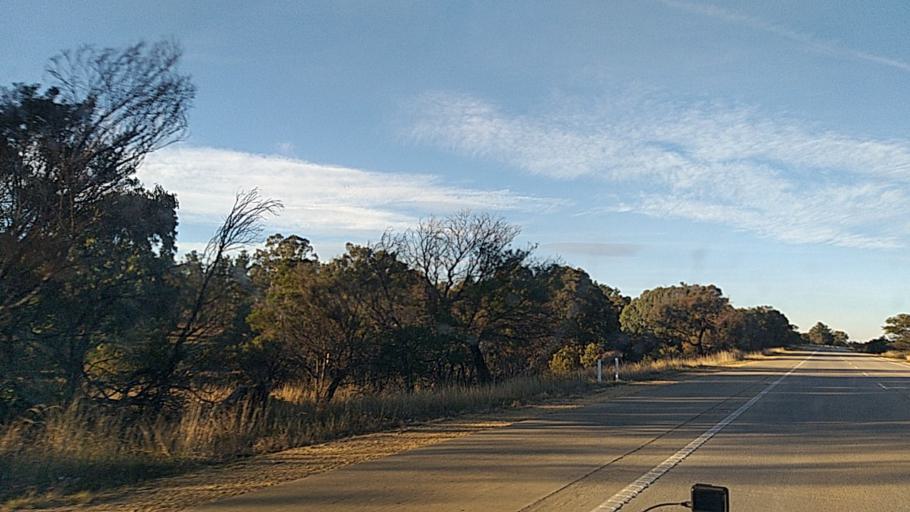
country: AU
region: New South Wales
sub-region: Yass Valley
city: Gundaroo
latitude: -35.1303
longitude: 149.3416
